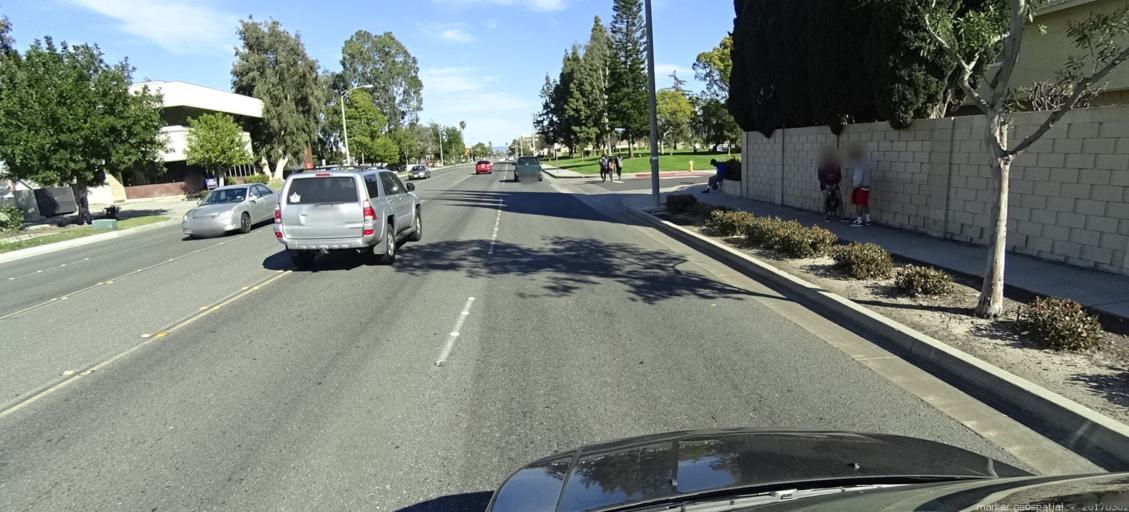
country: US
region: California
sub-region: Orange County
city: Stanton
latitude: 33.8246
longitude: -118.0000
